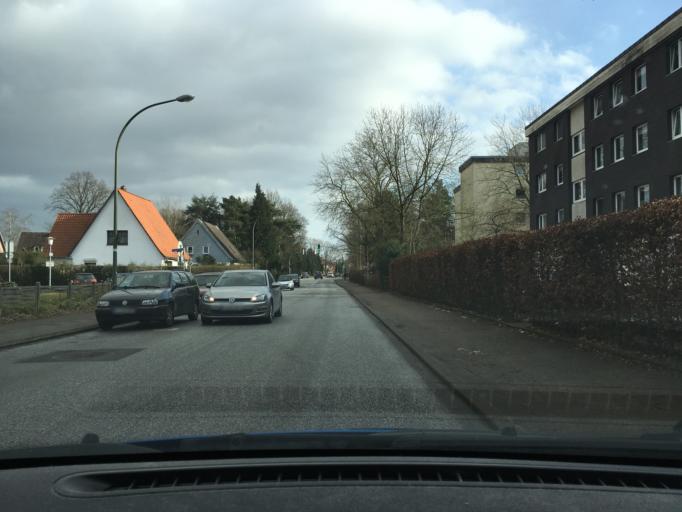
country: DE
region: Schleswig-Holstein
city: Wedel
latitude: 53.5745
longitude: 9.7191
